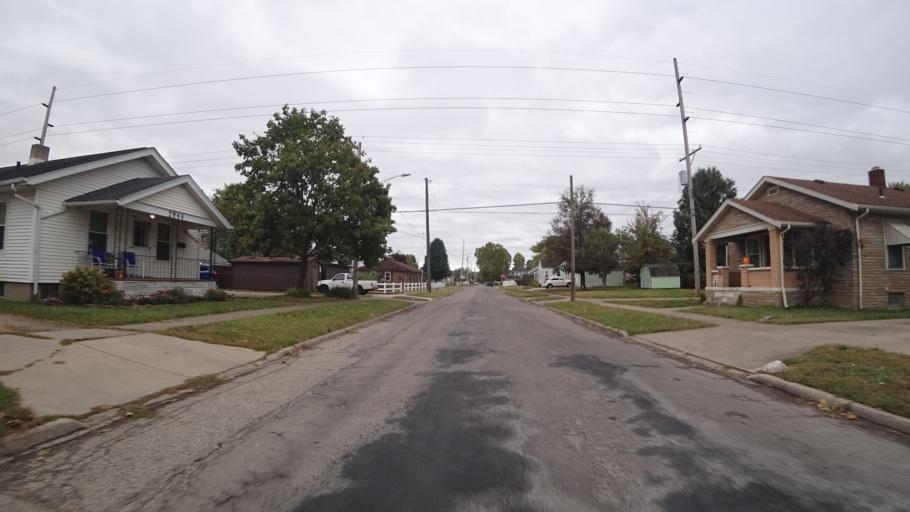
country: US
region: Ohio
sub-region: Butler County
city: Fairfield
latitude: 39.3678
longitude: -84.5606
